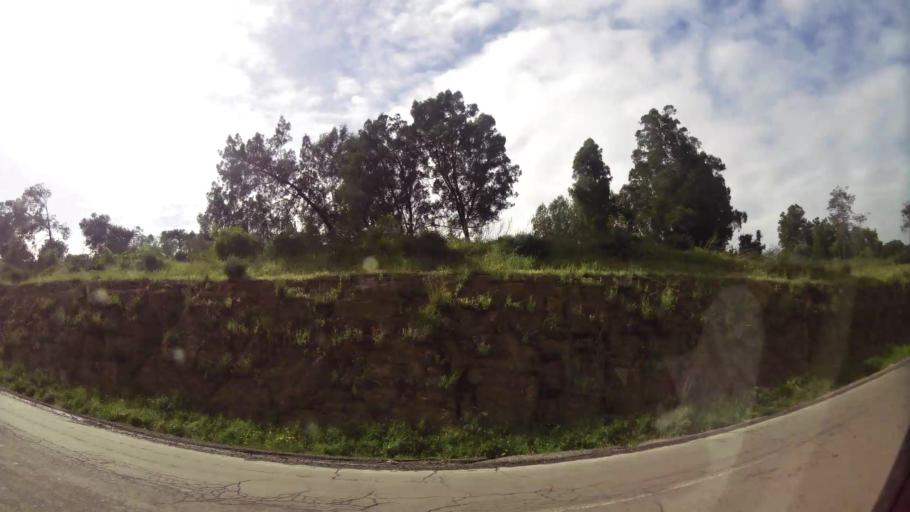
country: MA
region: Grand Casablanca
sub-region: Mohammedia
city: Mohammedia
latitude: 33.6554
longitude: -7.4004
